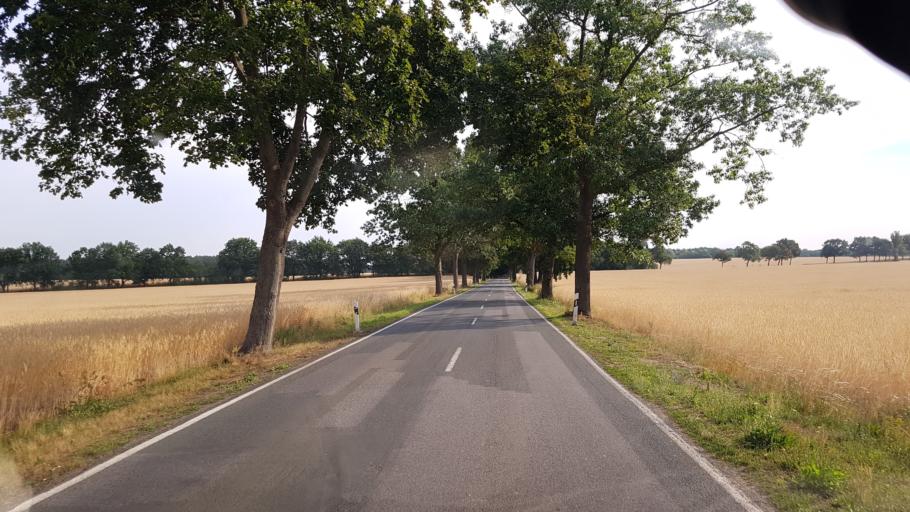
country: DE
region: Brandenburg
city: Golssen
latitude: 51.9630
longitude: 13.5434
